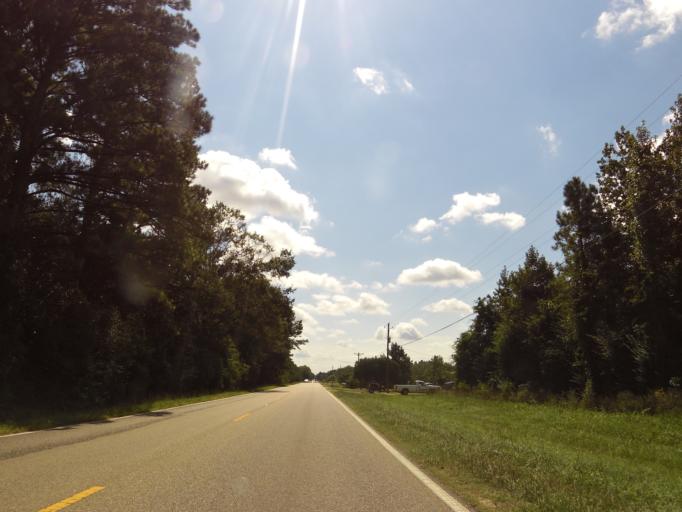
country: US
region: Alabama
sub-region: Dallas County
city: Selma
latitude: 32.4308
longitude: -87.0834
